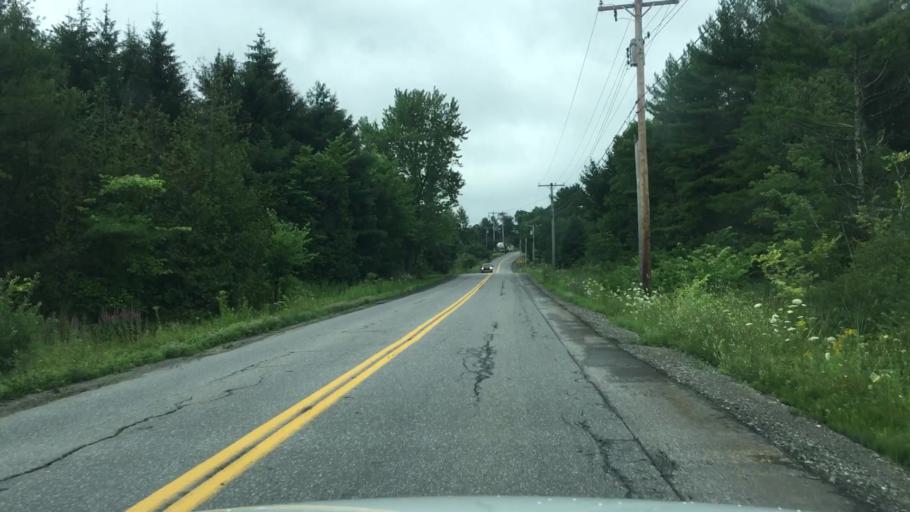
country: US
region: Maine
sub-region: Kennebec County
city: Augusta
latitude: 44.3239
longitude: -69.7334
